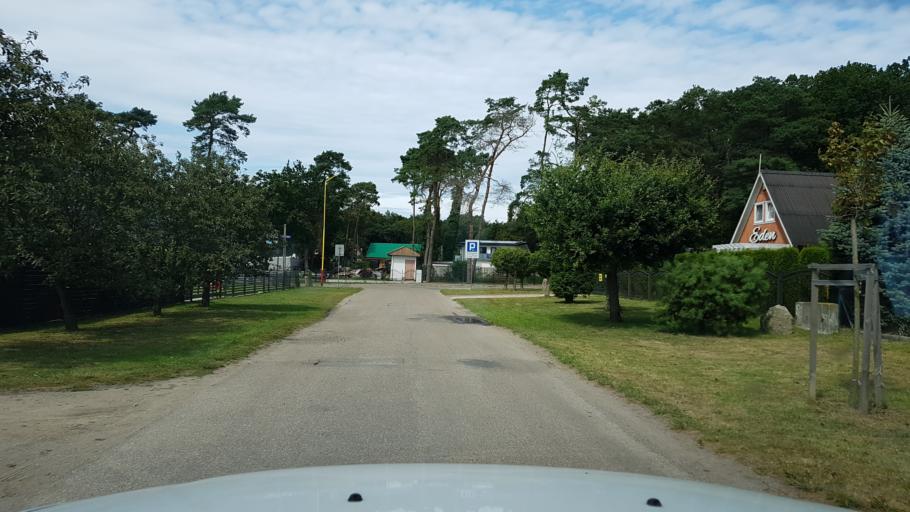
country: PL
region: West Pomeranian Voivodeship
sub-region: Powiat gryficki
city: Rewal
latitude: 54.0697
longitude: 14.9761
